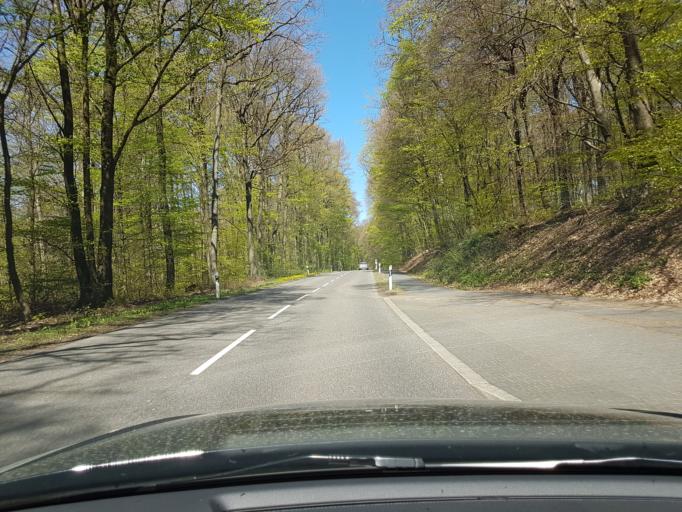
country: DE
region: Hesse
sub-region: Regierungsbezirk Darmstadt
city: Niedernhausen
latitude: 50.1739
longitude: 8.3005
